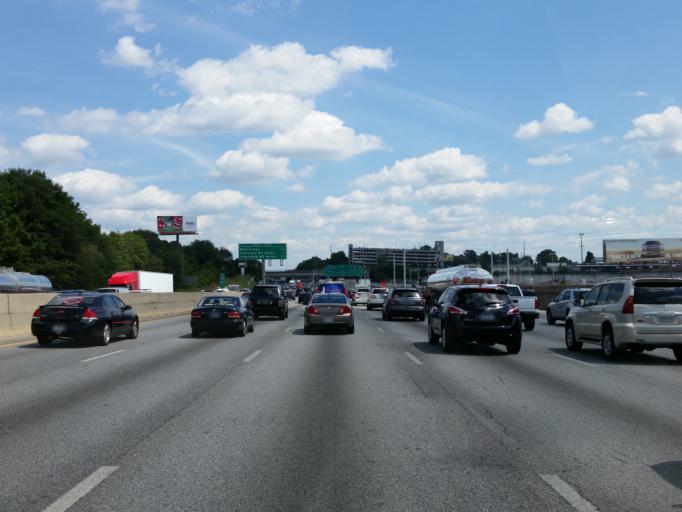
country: US
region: Georgia
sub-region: DeKalb County
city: Doraville
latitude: 33.9091
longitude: -84.2825
